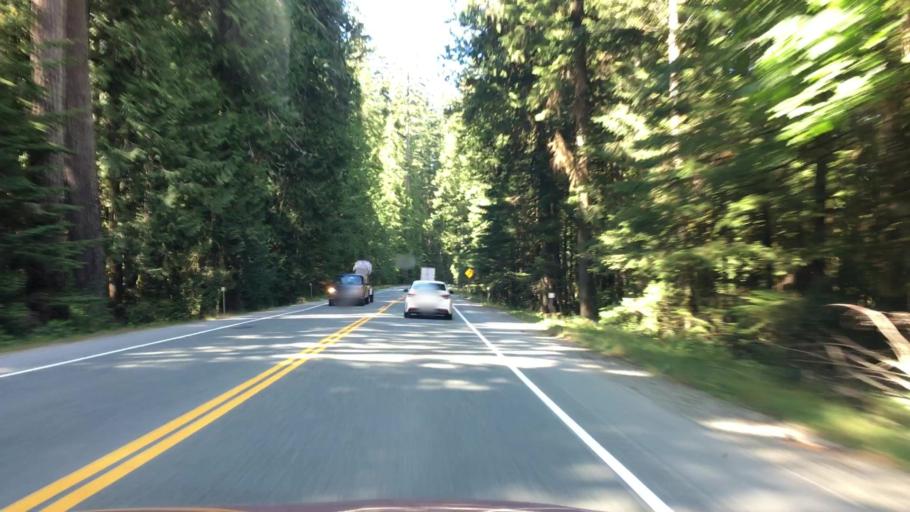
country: CA
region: British Columbia
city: Port Alberni
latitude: 49.2633
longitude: -124.6729
